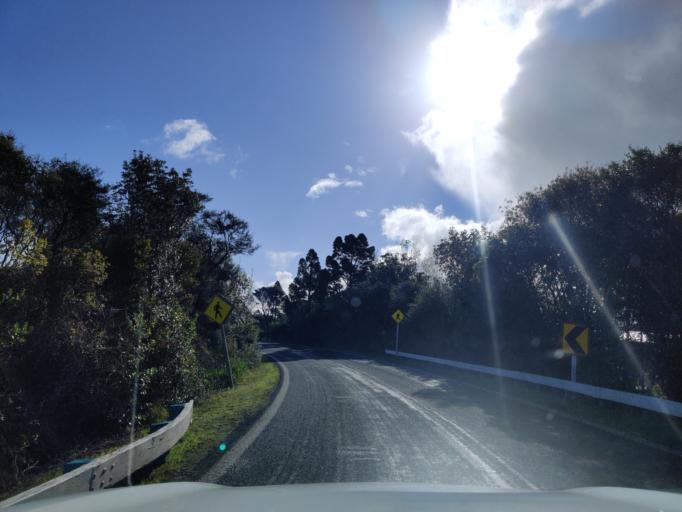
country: NZ
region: Waikato
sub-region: Thames-Coromandel District
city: Whitianga
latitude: -36.7231
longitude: 175.7294
